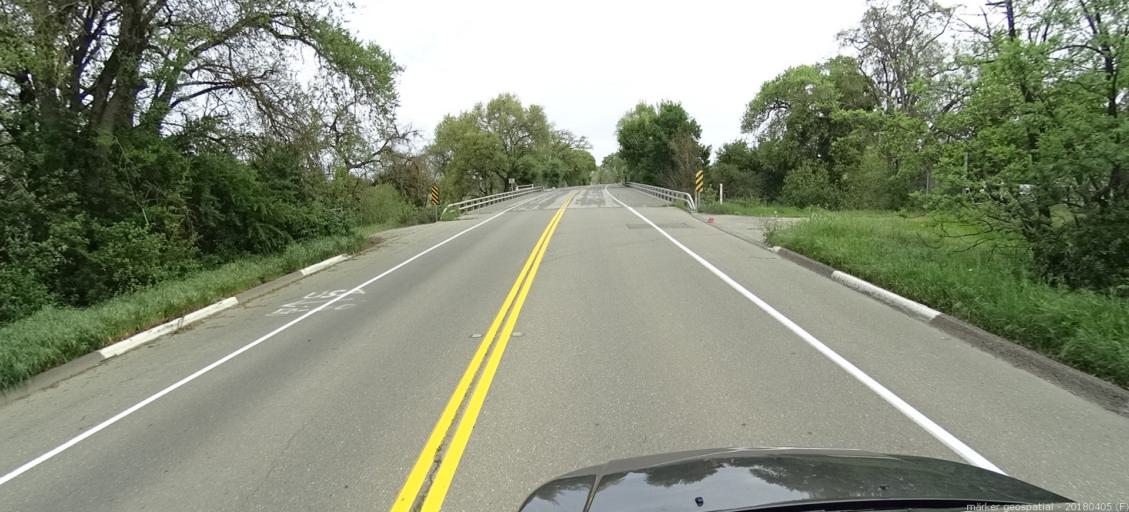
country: US
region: California
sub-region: San Joaquin County
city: Thornton
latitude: 38.2360
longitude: -121.4192
